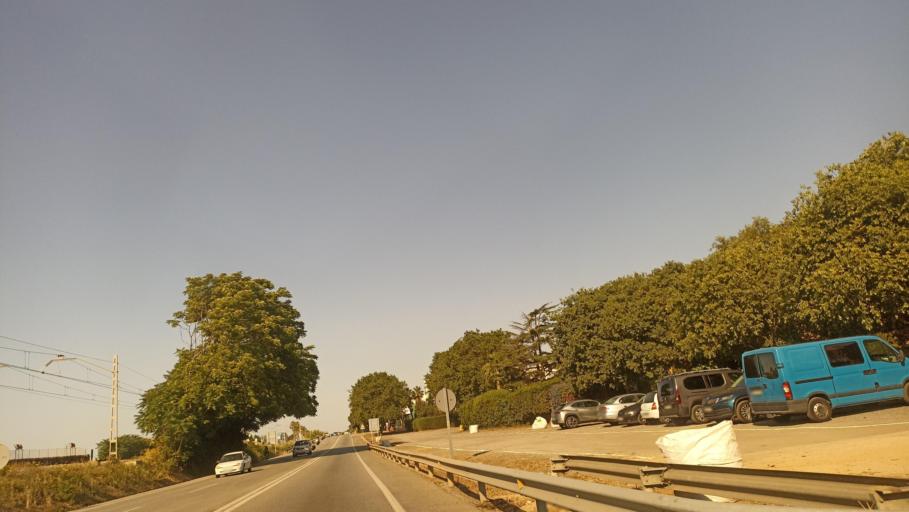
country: ES
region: Catalonia
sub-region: Provincia de Barcelona
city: Caldes d'Estrac
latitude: 41.5622
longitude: 2.5111
